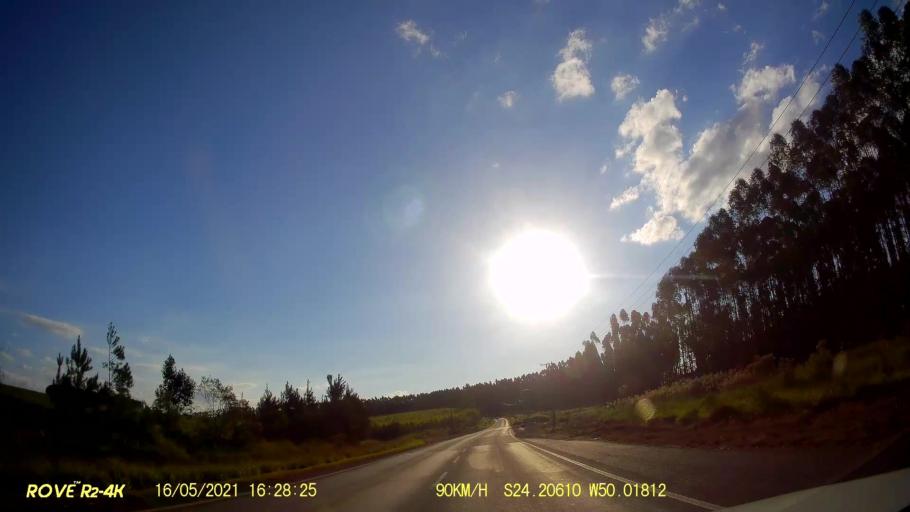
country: BR
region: Parana
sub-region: Jaguariaiva
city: Jaguariaiva
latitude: -24.2061
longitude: -50.0182
